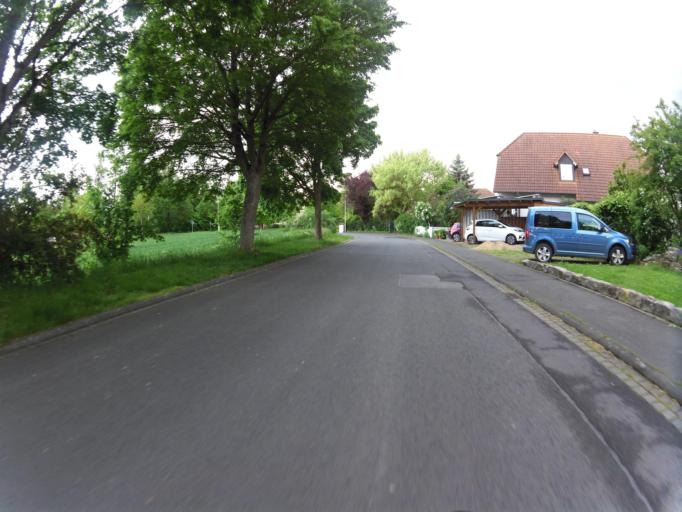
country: DE
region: Bavaria
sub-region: Regierungsbezirk Unterfranken
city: Volkach
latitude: 49.8694
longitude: 10.2290
